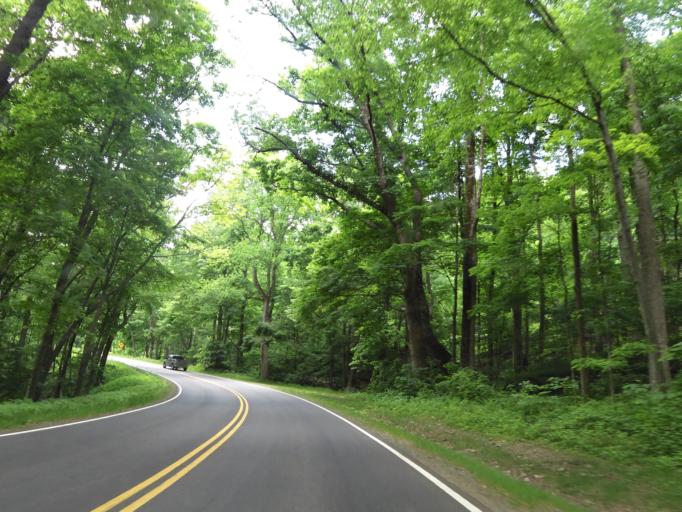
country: US
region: Tennessee
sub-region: Sevier County
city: Gatlinburg
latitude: 35.6408
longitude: -83.4962
